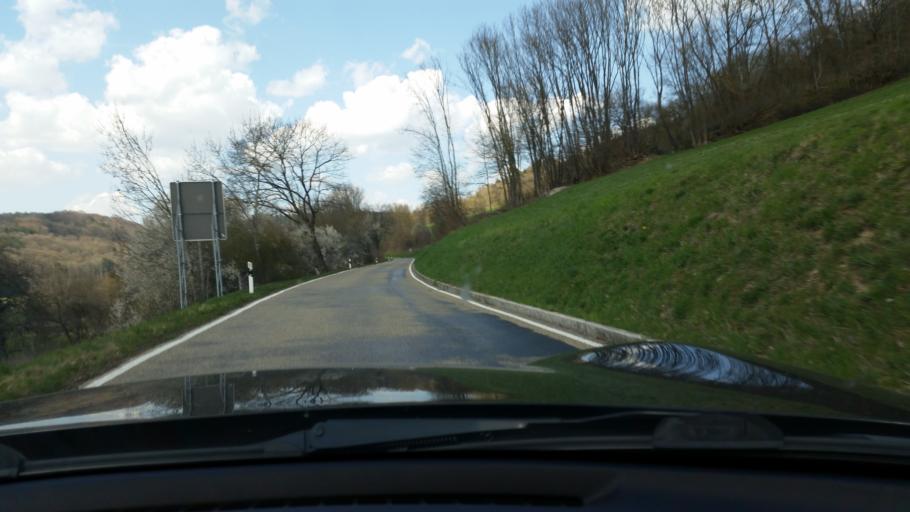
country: DE
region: Baden-Wuerttemberg
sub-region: Regierungsbezirk Stuttgart
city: Langenburg
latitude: 49.2651
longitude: 9.8420
